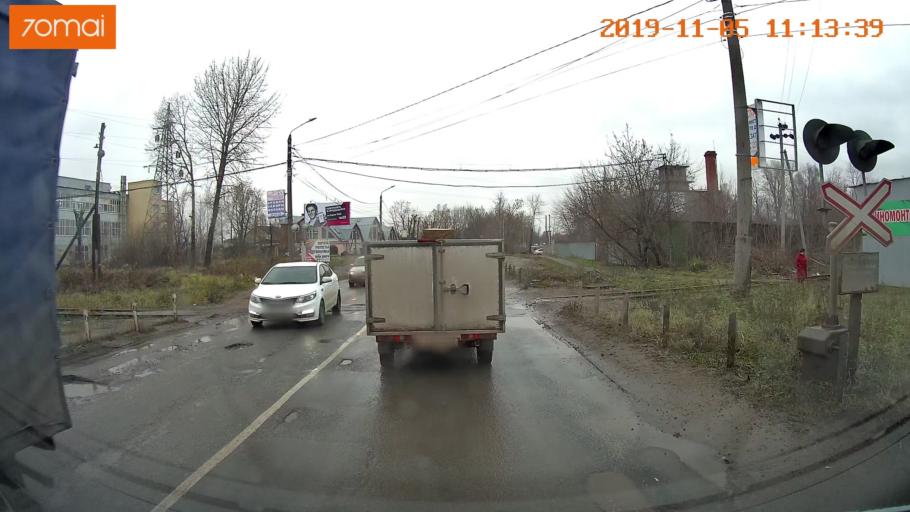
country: RU
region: Ivanovo
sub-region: Gorod Ivanovo
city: Ivanovo
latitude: 56.9671
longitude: 40.9523
